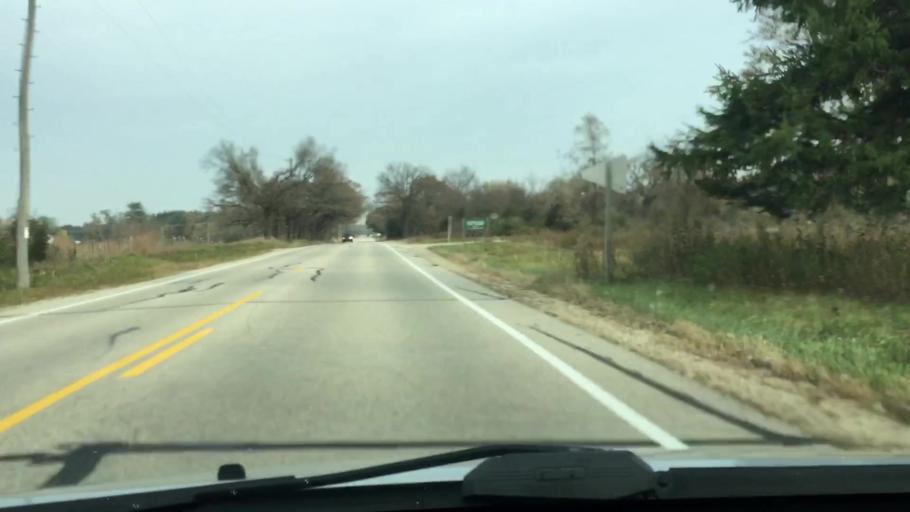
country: US
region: Wisconsin
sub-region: Waukesha County
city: Dousman
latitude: 42.9481
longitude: -88.4785
